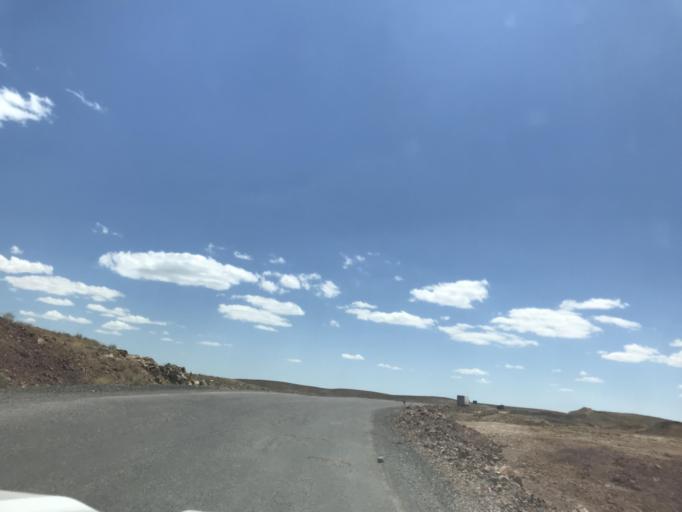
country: KZ
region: Almaty Oblysy
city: Ulken
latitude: 45.0629
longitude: 74.0014
